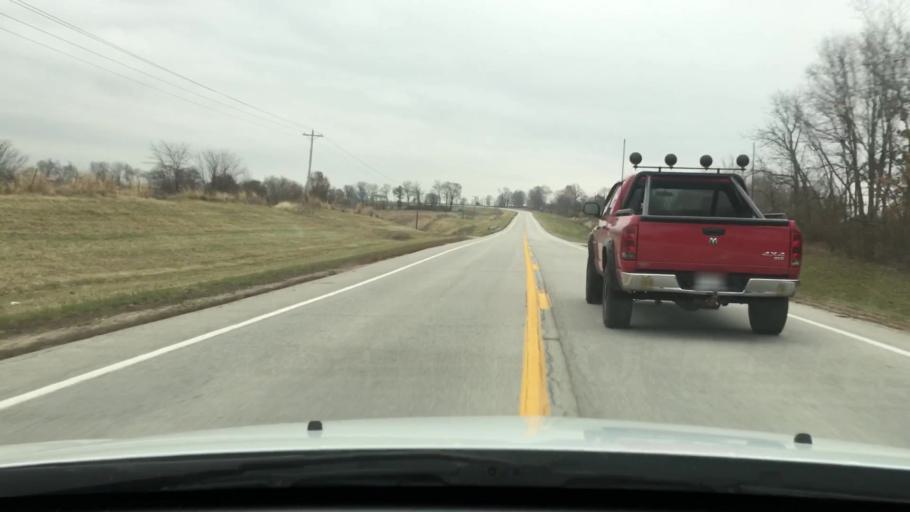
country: US
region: Missouri
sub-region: Pike County
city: Louisiana
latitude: 39.5274
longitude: -90.9304
